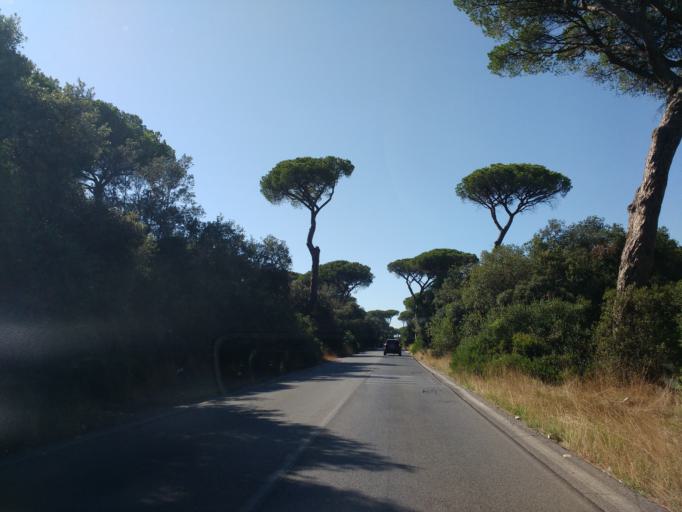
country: IT
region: Latium
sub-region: Citta metropolitana di Roma Capitale
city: Acilia-Castel Fusano-Ostia Antica
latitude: 41.7191
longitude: 12.3497
